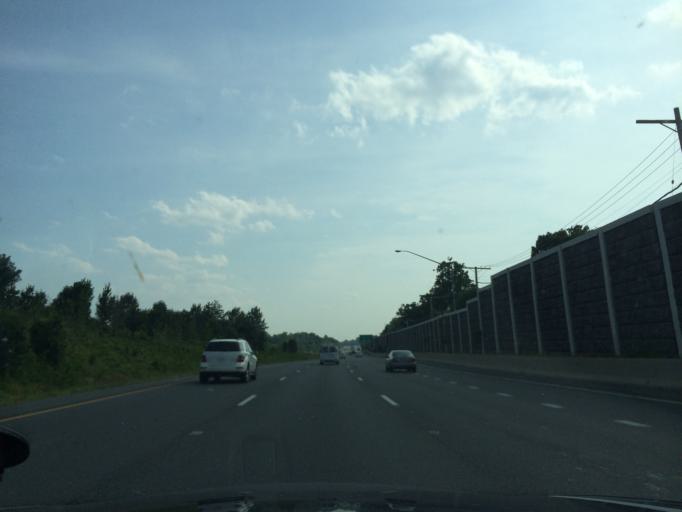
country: US
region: Maryland
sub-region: Howard County
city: Columbia
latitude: 39.2532
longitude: -76.8231
